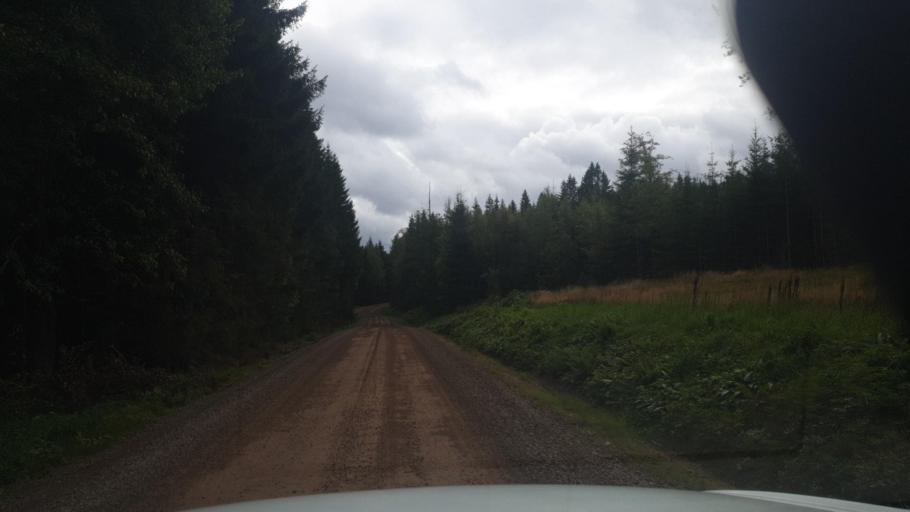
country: SE
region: Vaermland
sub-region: Arvika Kommun
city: Arvika
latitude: 59.9711
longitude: 12.6590
